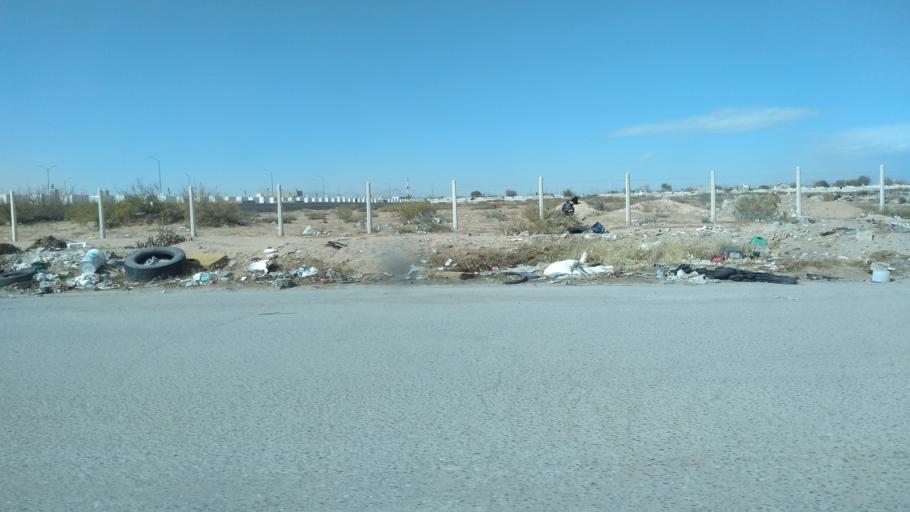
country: US
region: Texas
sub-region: El Paso County
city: San Elizario
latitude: 31.5807
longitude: -106.3490
